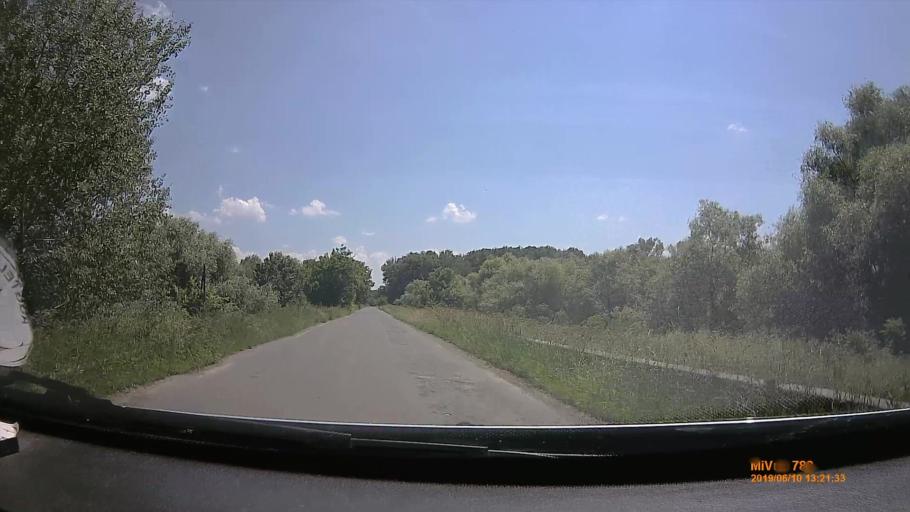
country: HU
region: Borsod-Abauj-Zemplen
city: Tiszaluc
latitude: 48.0356
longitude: 21.0768
